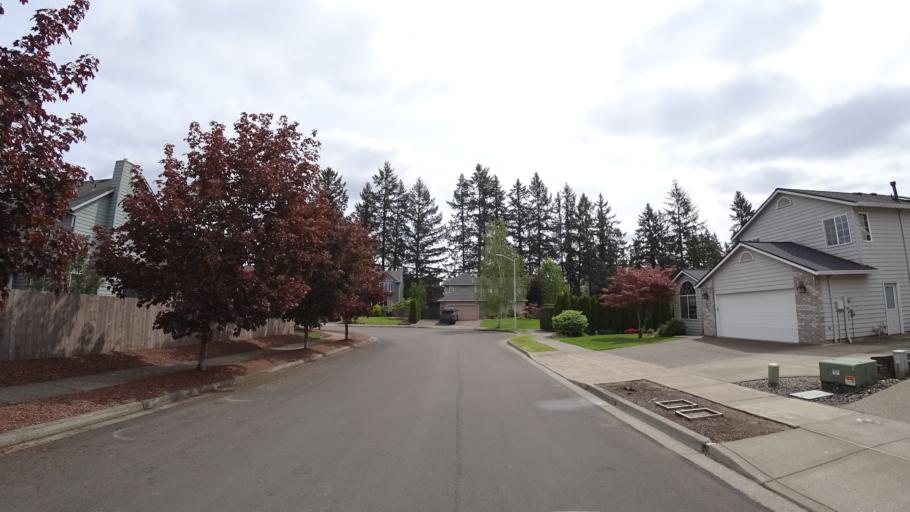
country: US
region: Oregon
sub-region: Washington County
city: Hillsboro
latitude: 45.5438
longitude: -122.9905
